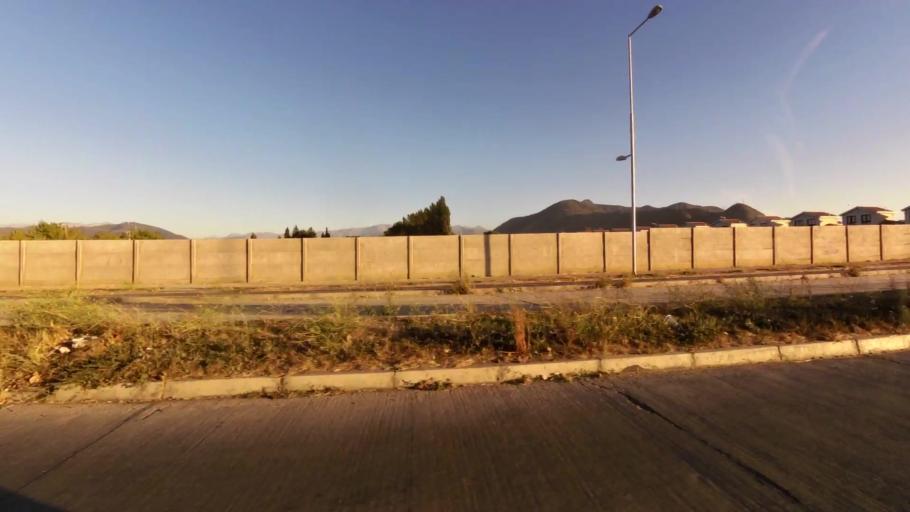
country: CL
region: O'Higgins
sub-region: Provincia de Cachapoal
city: Rancagua
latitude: -34.1884
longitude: -70.7349
